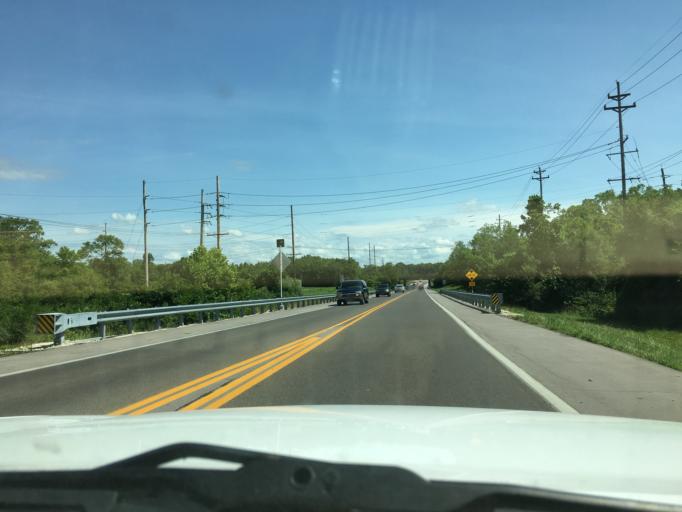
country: US
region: Missouri
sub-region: Franklin County
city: Union
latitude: 38.4536
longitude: -91.0018
